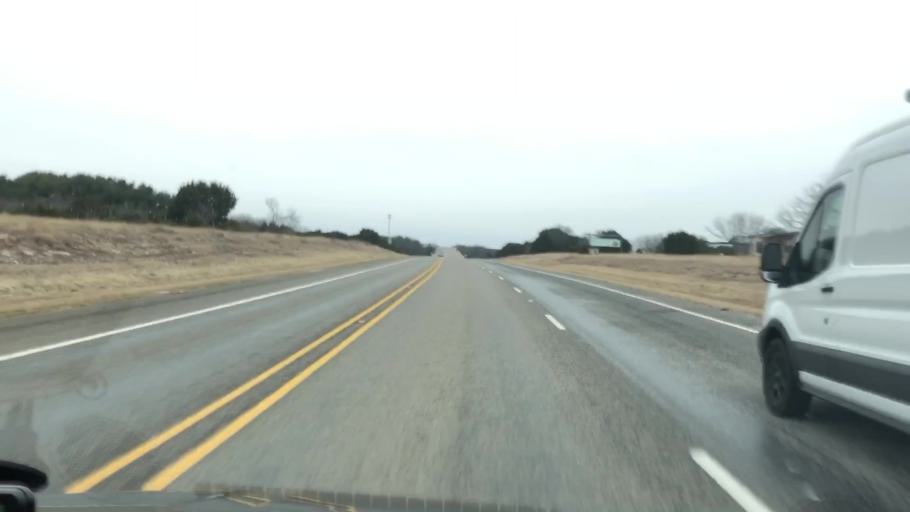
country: US
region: Texas
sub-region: Lampasas County
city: Lampasas
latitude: 31.1691
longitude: -98.1747
